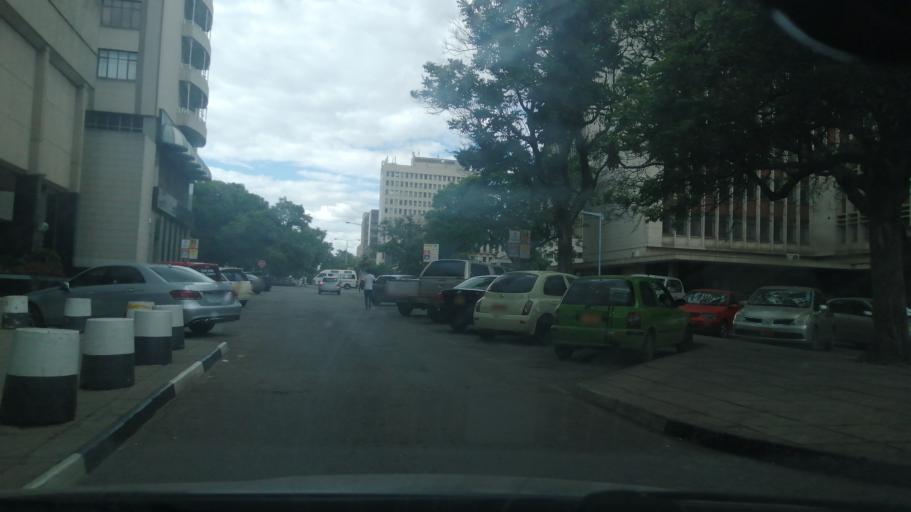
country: ZW
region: Harare
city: Harare
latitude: -17.8308
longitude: 31.0531
